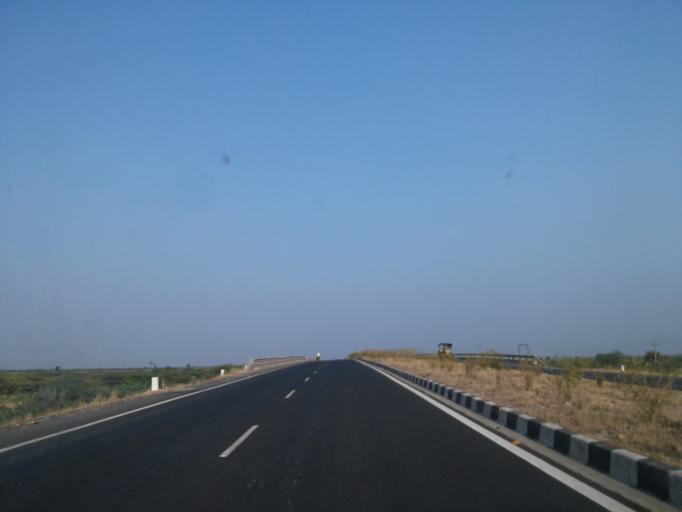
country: IN
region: Gujarat
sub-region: Surendranagar
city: Dhrangadhra
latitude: 23.0267
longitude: 71.6440
